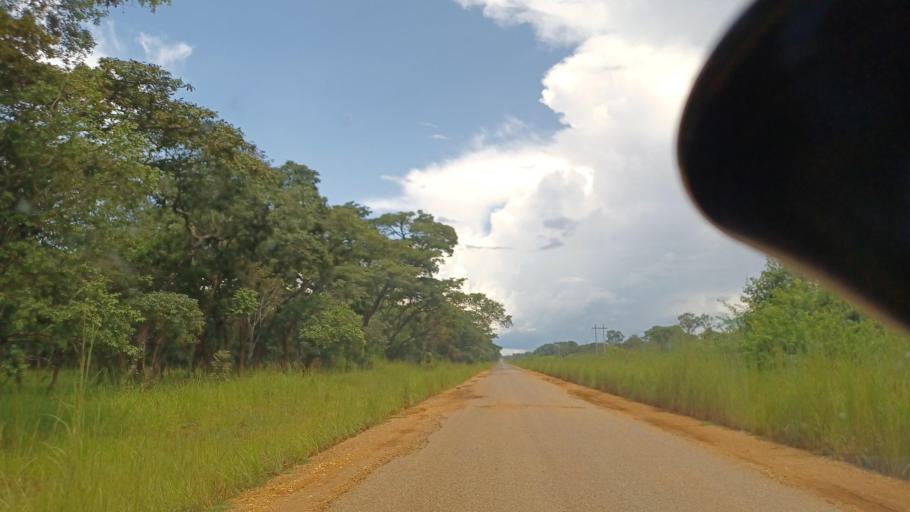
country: ZM
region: North-Western
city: Kasempa
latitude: -12.8829
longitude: 26.0467
